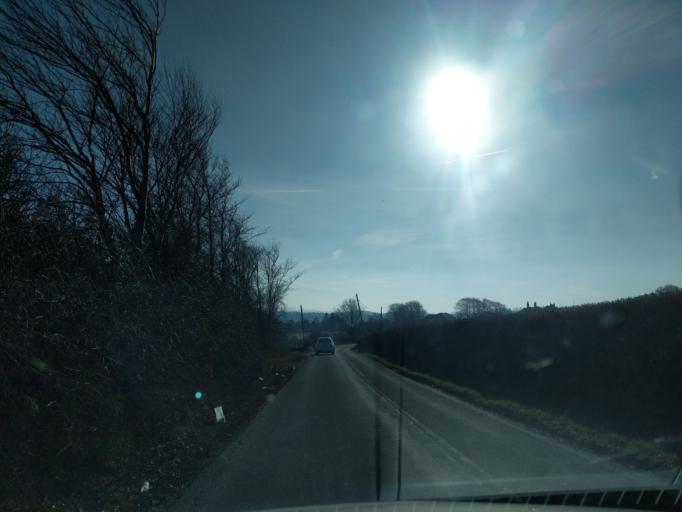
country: GB
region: Scotland
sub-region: South Lanarkshire
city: Lanark
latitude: 55.6851
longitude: -3.8217
